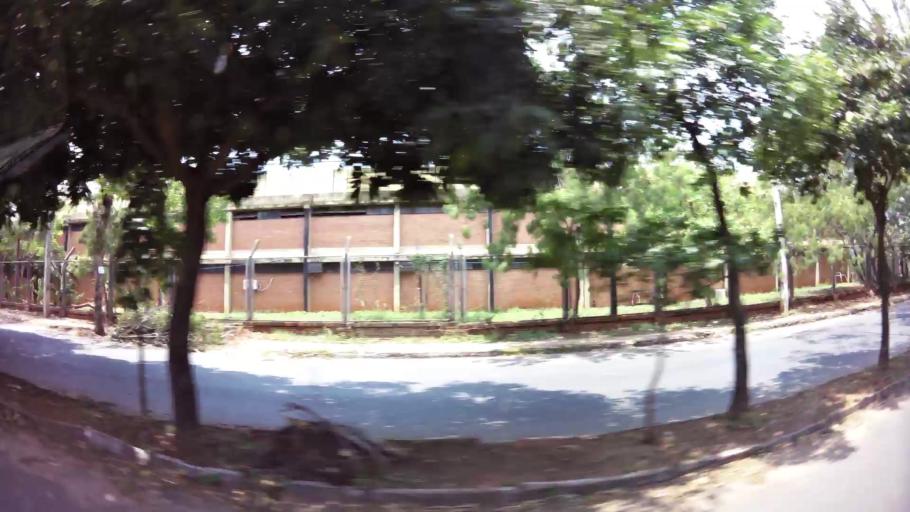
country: PY
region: Central
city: Lambare
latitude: -25.3097
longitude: -57.5685
